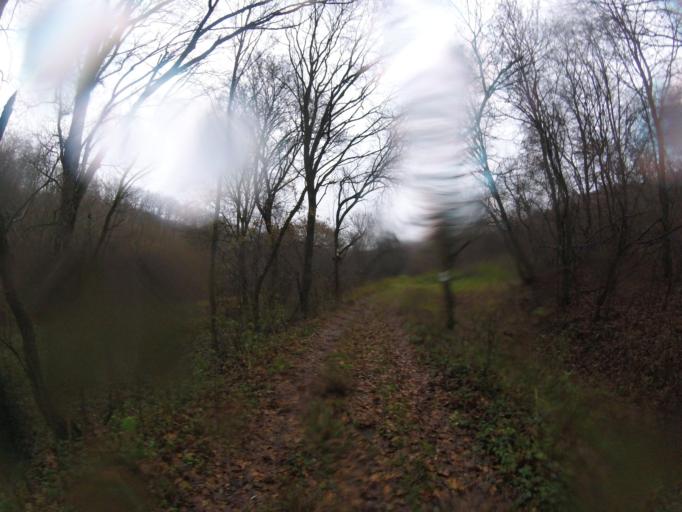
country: HU
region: Pest
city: Szob
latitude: 47.8550
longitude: 18.8459
